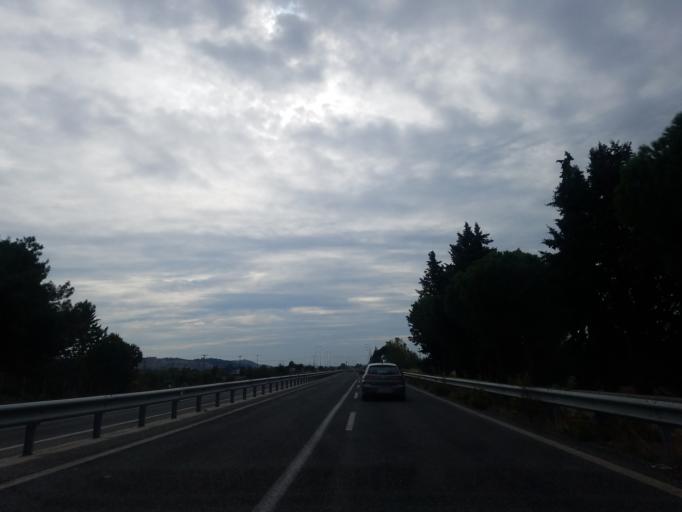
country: GR
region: Thessaly
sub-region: Trikala
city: Vasiliki
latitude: 39.6666
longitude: 21.6690
